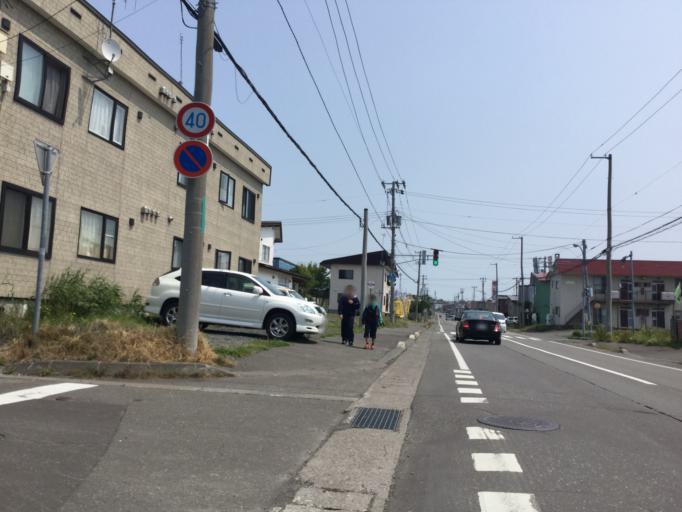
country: JP
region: Hokkaido
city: Wakkanai
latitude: 45.3864
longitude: 141.7091
